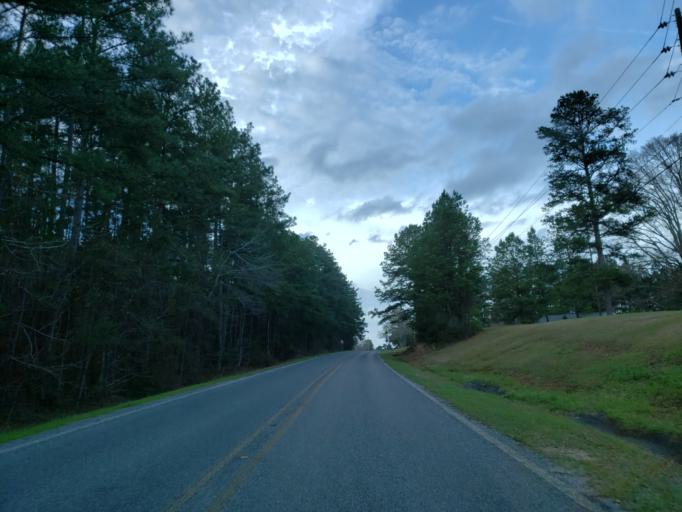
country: US
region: Mississippi
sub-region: Clarke County
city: Stonewall
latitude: 32.2221
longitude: -88.7001
